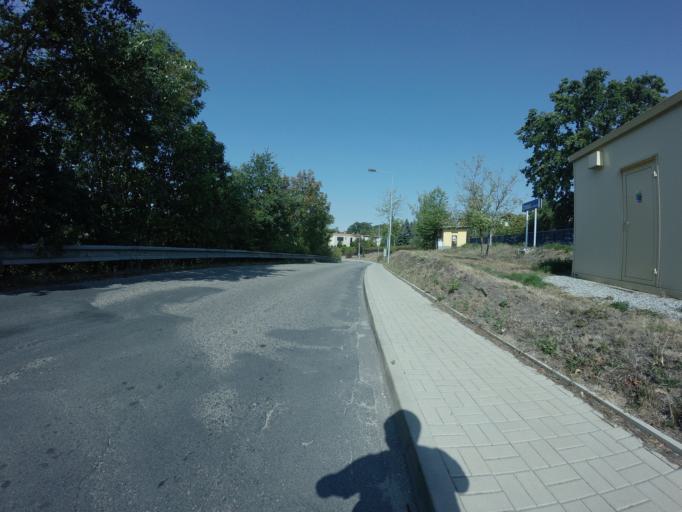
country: CZ
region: Central Bohemia
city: Tynec nad Sazavou
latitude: 49.8393
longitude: 14.5773
